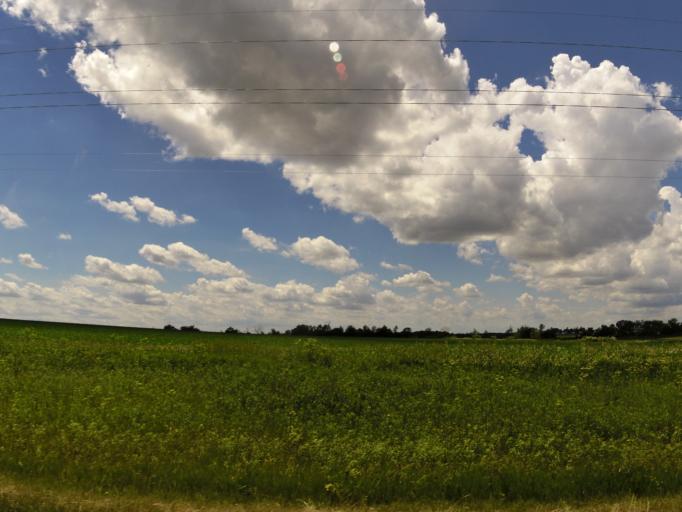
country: US
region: Iowa
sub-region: Buchanan County
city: Independence
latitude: 42.5519
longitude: -91.9050
